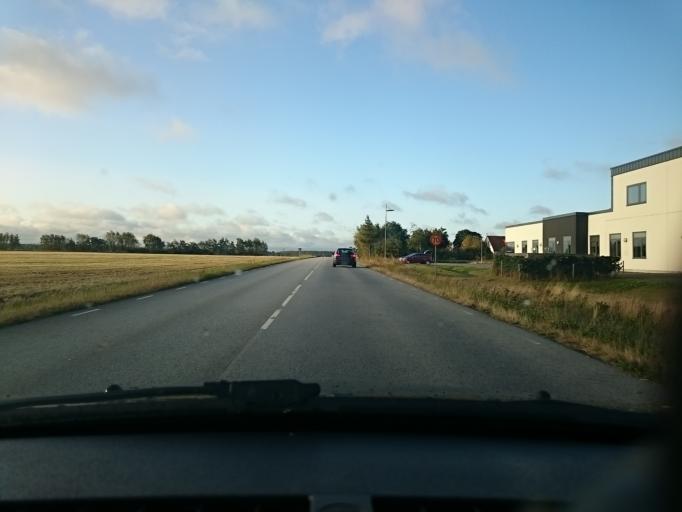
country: SE
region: Skane
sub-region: Kavlinge Kommun
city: Hofterup
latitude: 55.7743
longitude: 12.9654
